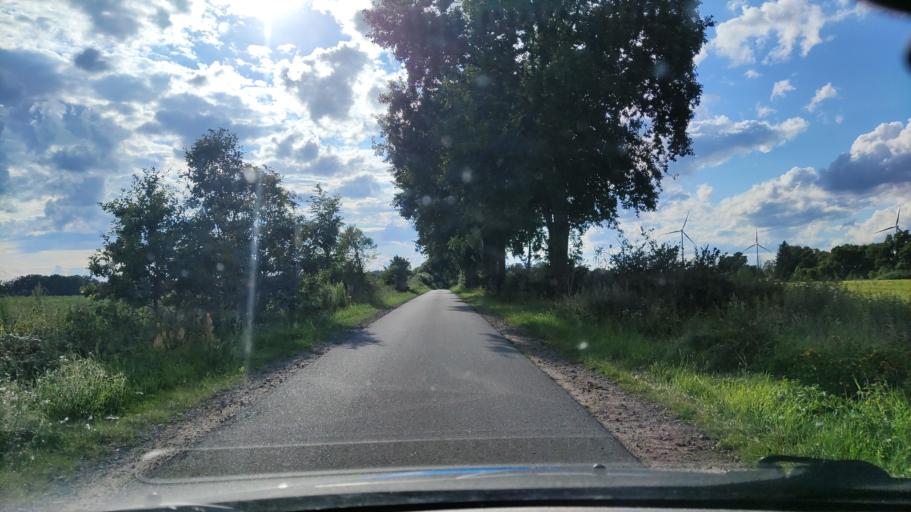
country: DE
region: Lower Saxony
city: Nahrendorf
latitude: 53.1791
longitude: 10.7926
